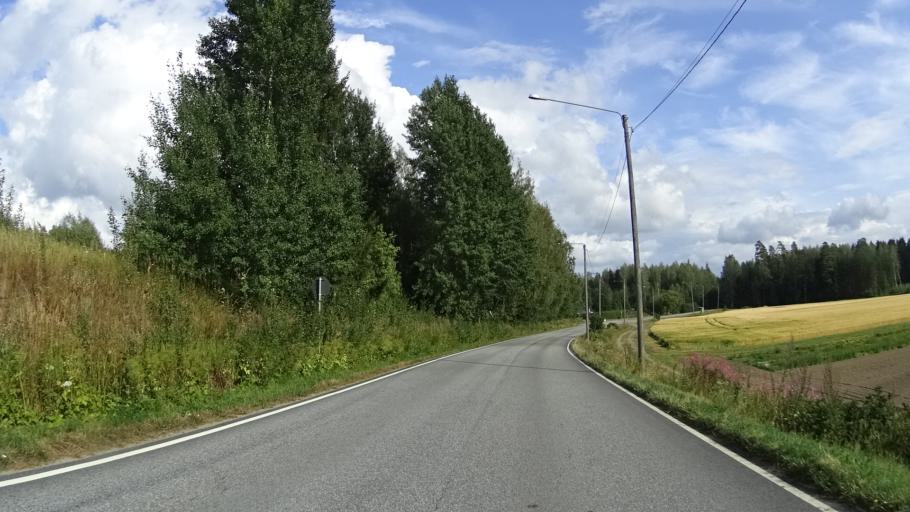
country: FI
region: Pirkanmaa
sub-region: Tampere
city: Paelkaene
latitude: 61.3531
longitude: 24.2282
